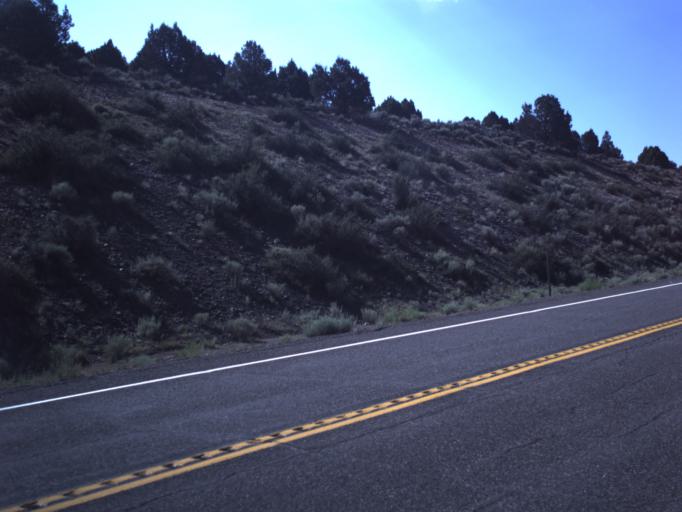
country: US
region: Utah
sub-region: Wayne County
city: Loa
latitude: 38.5091
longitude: -111.8321
